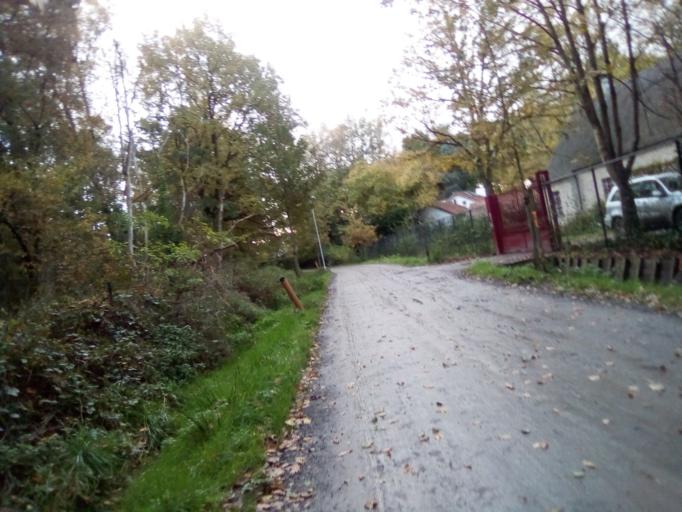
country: BE
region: Flanders
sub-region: Provincie Oost-Vlaanderen
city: Lokeren
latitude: 51.1207
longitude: 3.9991
